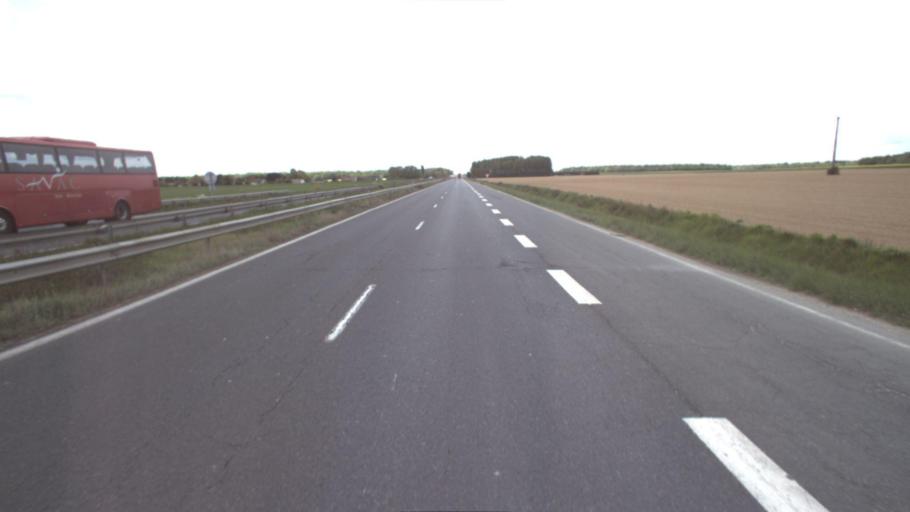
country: FR
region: Ile-de-France
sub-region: Departement de Seine-et-Marne
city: Rozay-en-Brie
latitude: 48.6860
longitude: 2.9333
